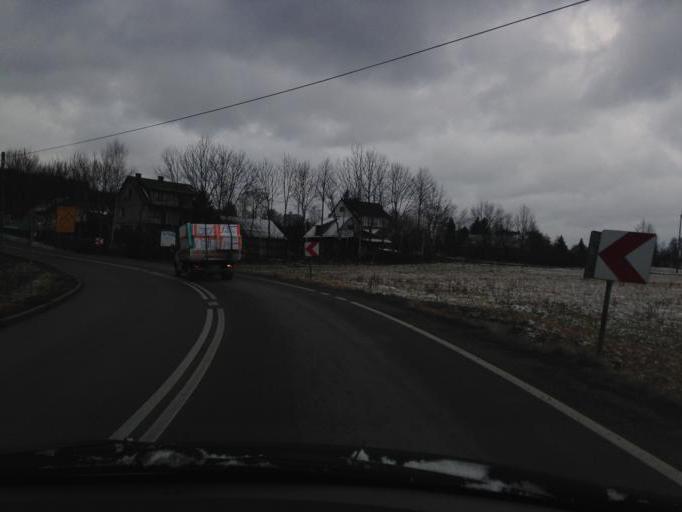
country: PL
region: Lesser Poland Voivodeship
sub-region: Powiat bochenski
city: Trzciana
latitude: 49.8574
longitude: 20.3393
